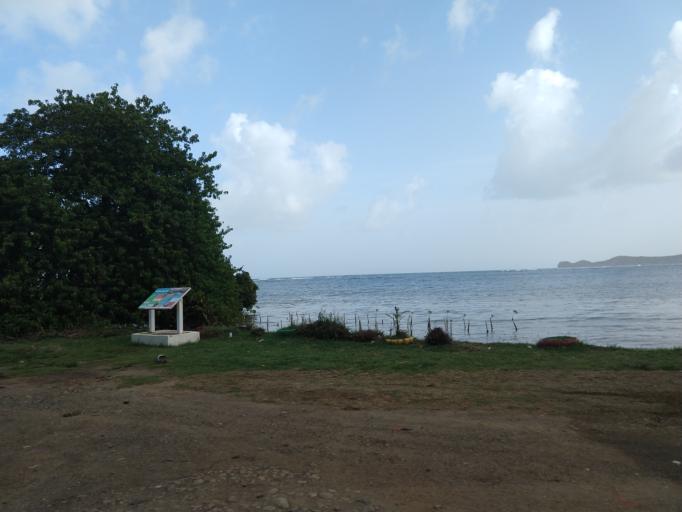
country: GD
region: Saint Andrew
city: Grenville
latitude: 12.1248
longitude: -61.6172
